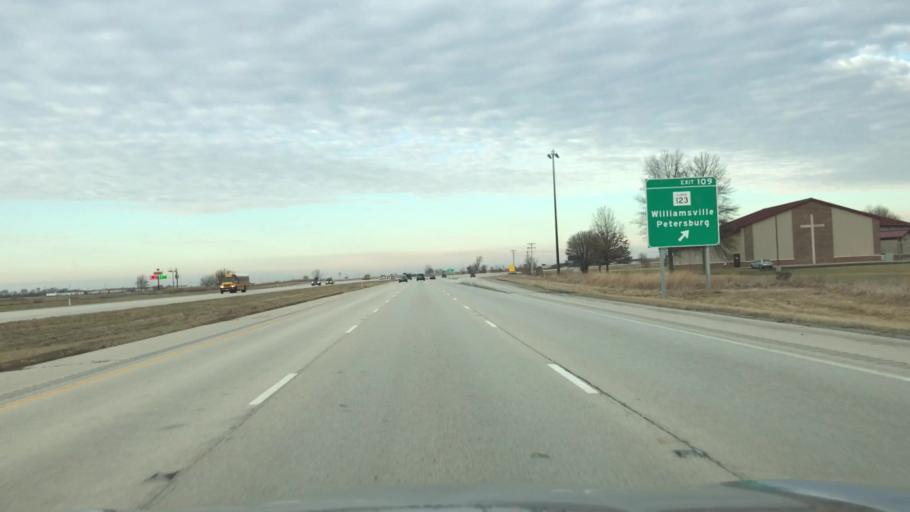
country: US
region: Illinois
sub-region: Sangamon County
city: Williamsville
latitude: 39.9512
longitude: -89.5574
